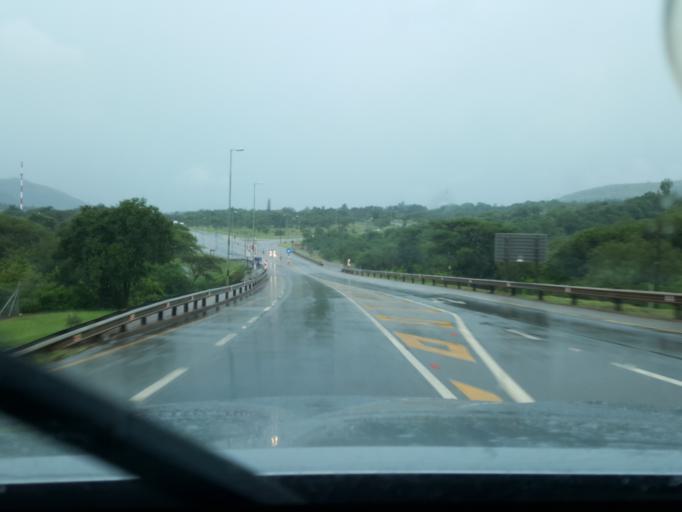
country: ZA
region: Mpumalanga
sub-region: Ehlanzeni District
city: Nelspruit
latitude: -25.5776
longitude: 30.6661
